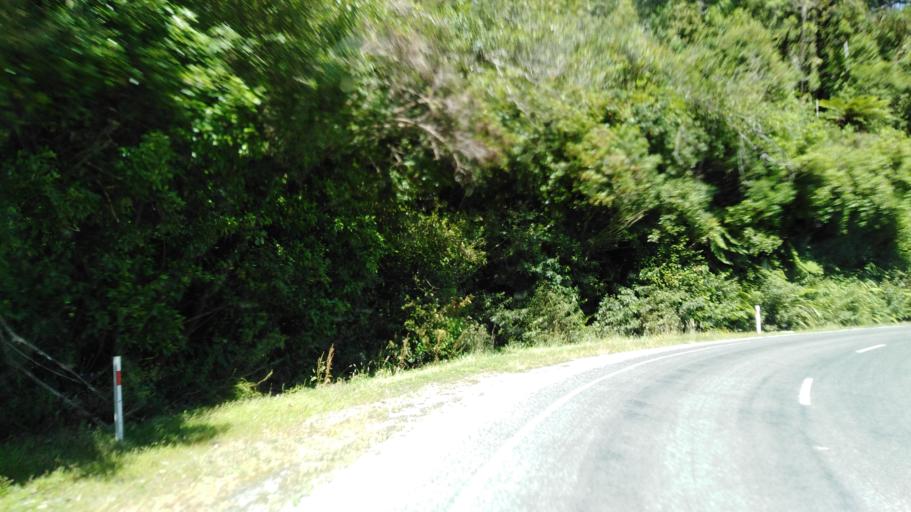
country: NZ
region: West Coast
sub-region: Buller District
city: Westport
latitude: -41.4934
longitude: 172.0500
